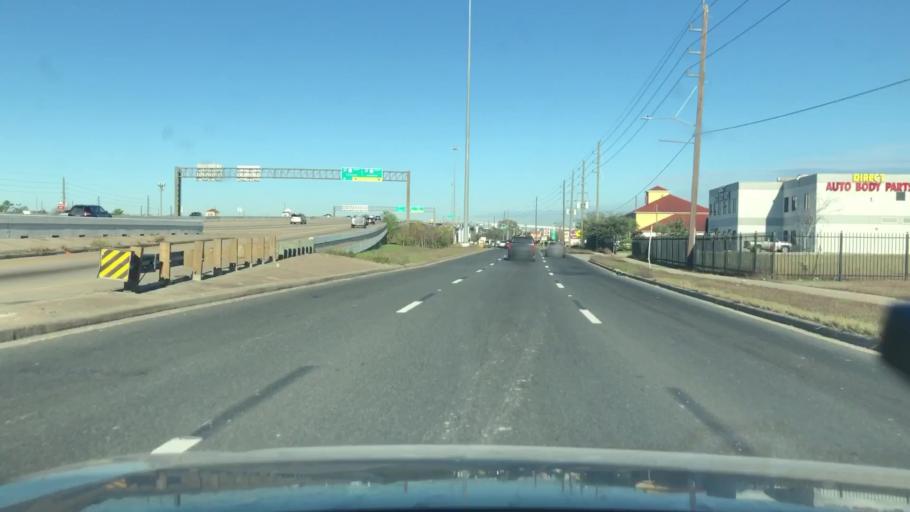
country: US
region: Texas
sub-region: Fort Bend County
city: Missouri City
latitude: 29.6520
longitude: -95.5478
